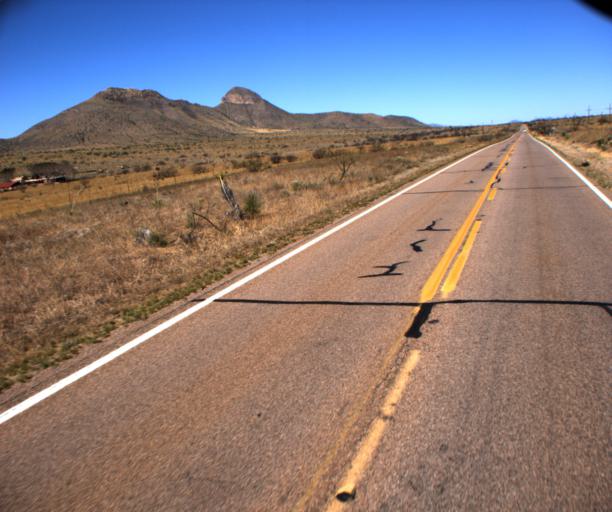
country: US
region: Arizona
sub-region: Cochise County
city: Huachuca City
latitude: 31.7117
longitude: -110.4542
